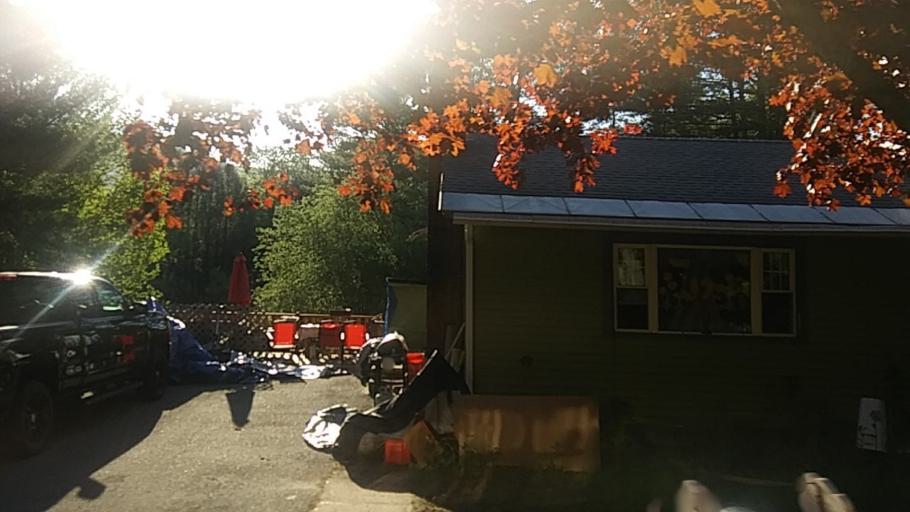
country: US
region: Massachusetts
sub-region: Franklin County
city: Shelburne Falls
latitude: 42.5987
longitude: -72.7442
